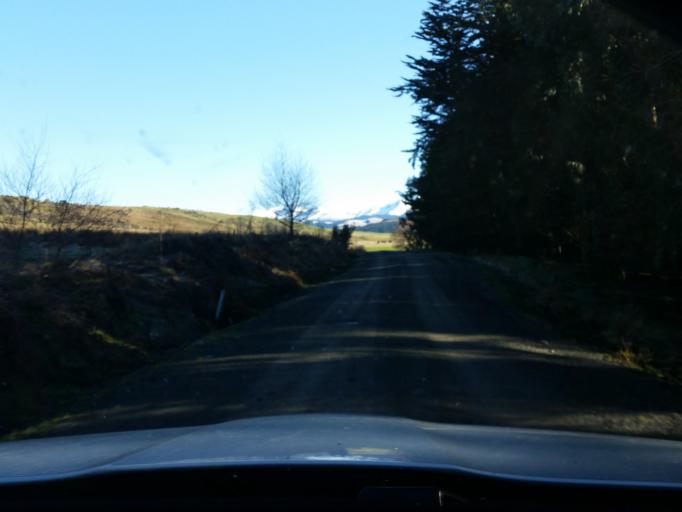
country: NZ
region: Southland
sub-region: Southland District
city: Winton
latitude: -45.7251
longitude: 168.0951
